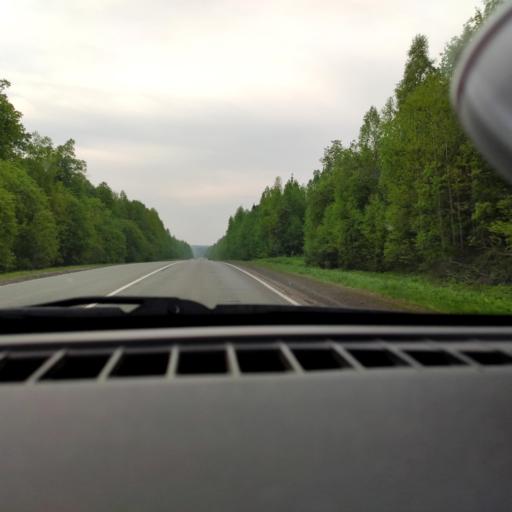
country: RU
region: Perm
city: Perm
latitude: 58.1763
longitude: 56.2294
